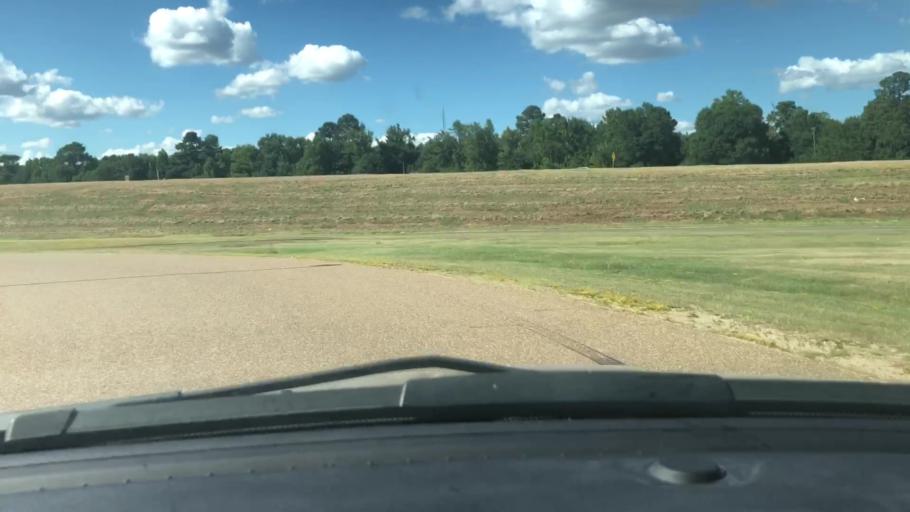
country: US
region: Texas
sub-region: Bowie County
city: Wake Village
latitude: 33.3851
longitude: -94.0881
